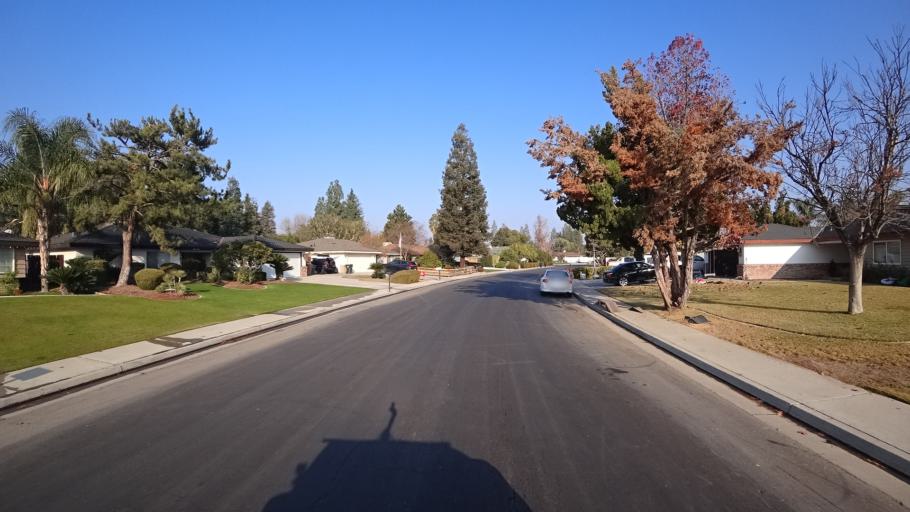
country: US
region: California
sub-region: Kern County
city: Greenacres
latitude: 35.3403
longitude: -119.0836
